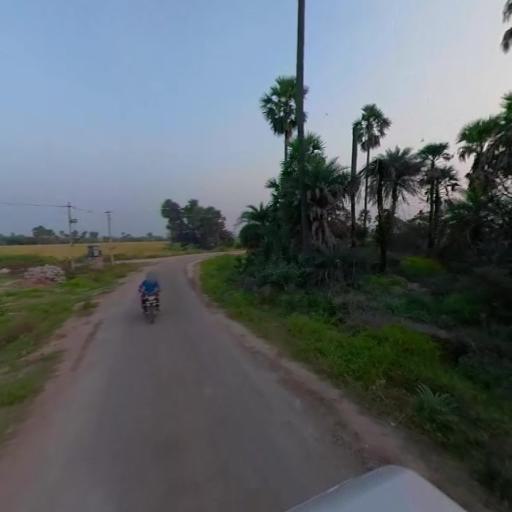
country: IN
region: Telangana
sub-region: Nalgonda
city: Suriapet
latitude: 17.0620
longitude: 79.5472
